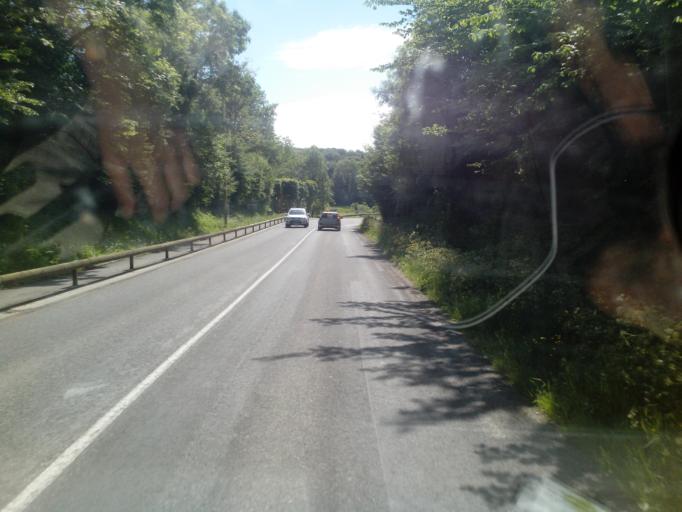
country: FR
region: Haute-Normandie
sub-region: Departement de l'Eure
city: Beuzeville
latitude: 49.3419
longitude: 0.3341
